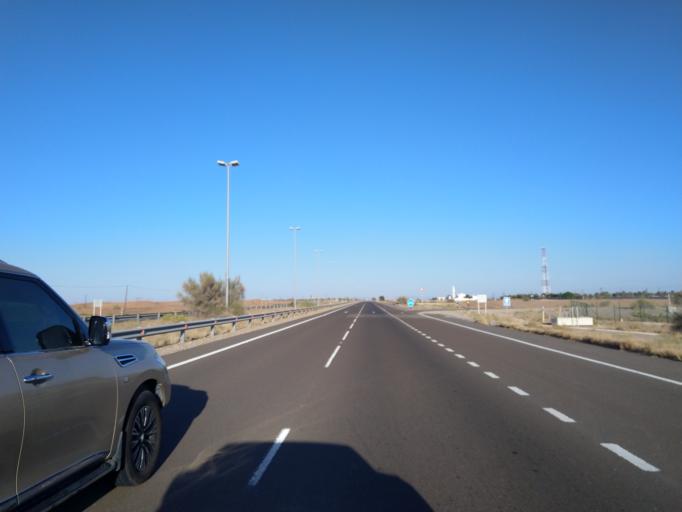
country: OM
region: Al Buraimi
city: Al Buraymi
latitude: 24.5401
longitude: 55.6282
